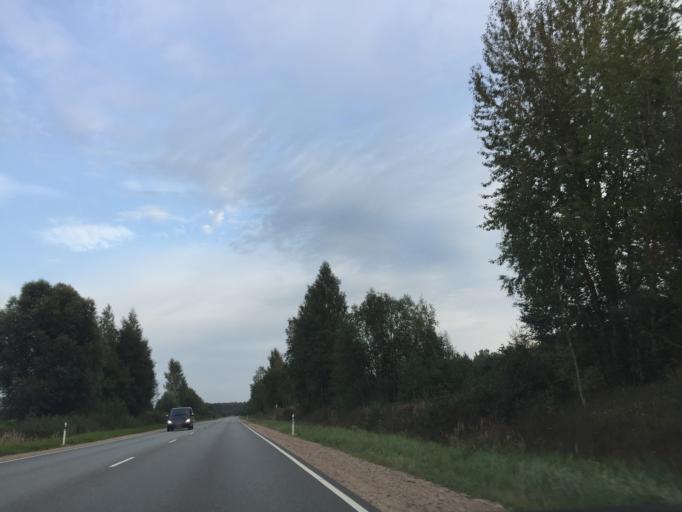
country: LV
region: Kekava
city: Kekava
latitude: 56.7936
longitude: 24.2800
